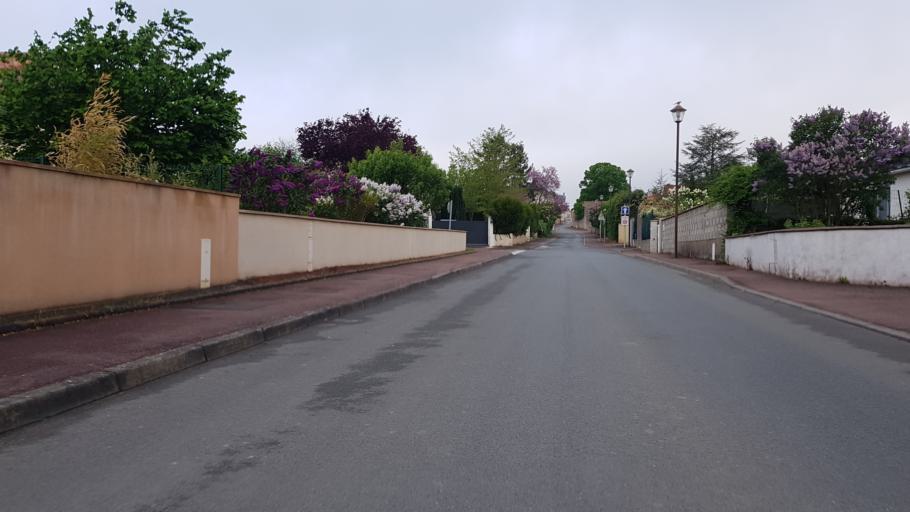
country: FR
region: Poitou-Charentes
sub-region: Departement de la Vienne
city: Jaunay-Clan
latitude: 46.6749
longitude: 0.3725
